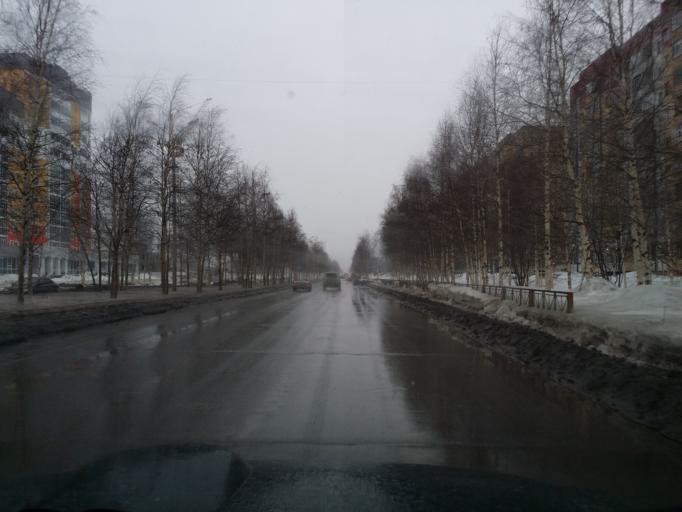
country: RU
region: Khanty-Mansiyskiy Avtonomnyy Okrug
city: Nizhnevartovsk
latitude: 60.9300
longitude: 76.5855
